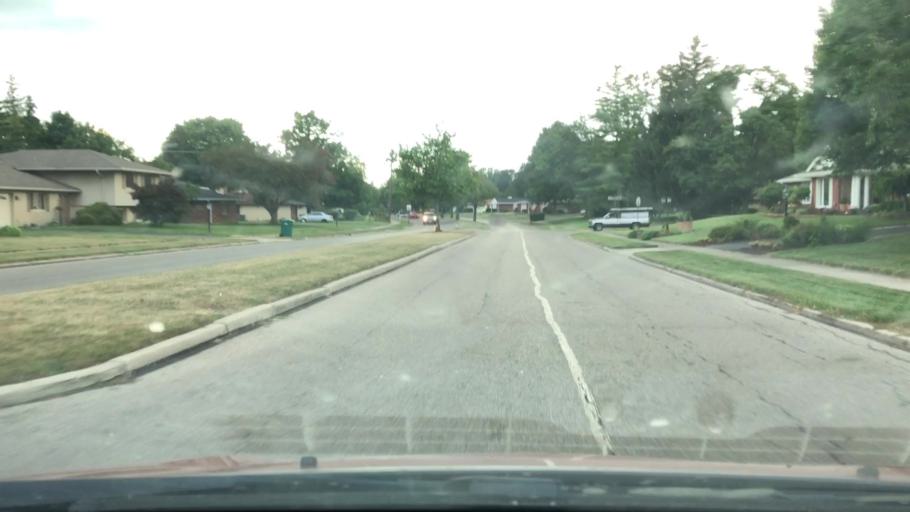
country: US
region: Ohio
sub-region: Montgomery County
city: Centerville
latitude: 39.6621
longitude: -84.1187
